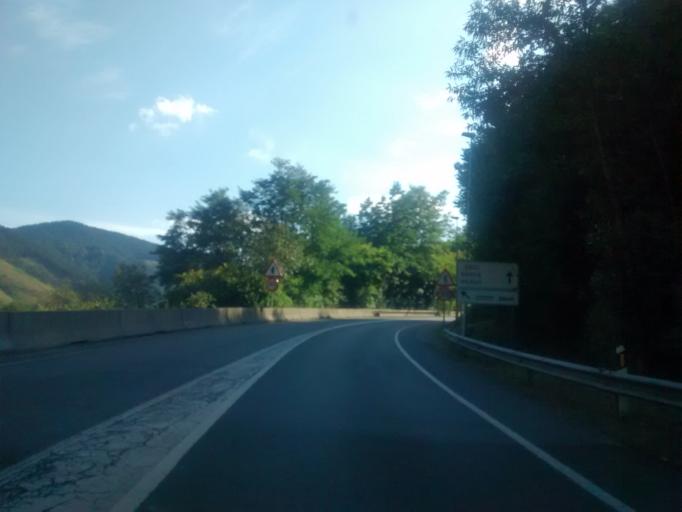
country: ES
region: Basque Country
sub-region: Provincia de Guipuzcoa
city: Eibar
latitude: 43.1903
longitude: -2.4674
